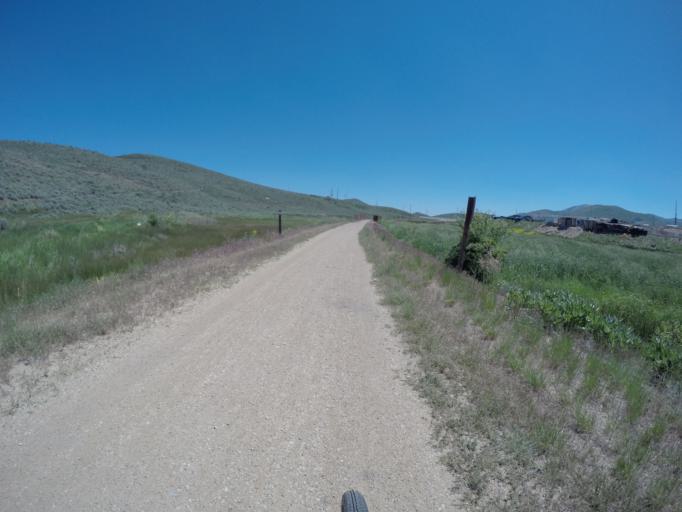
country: US
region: Utah
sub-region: Summit County
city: Park City
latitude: 40.6894
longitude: -111.4581
